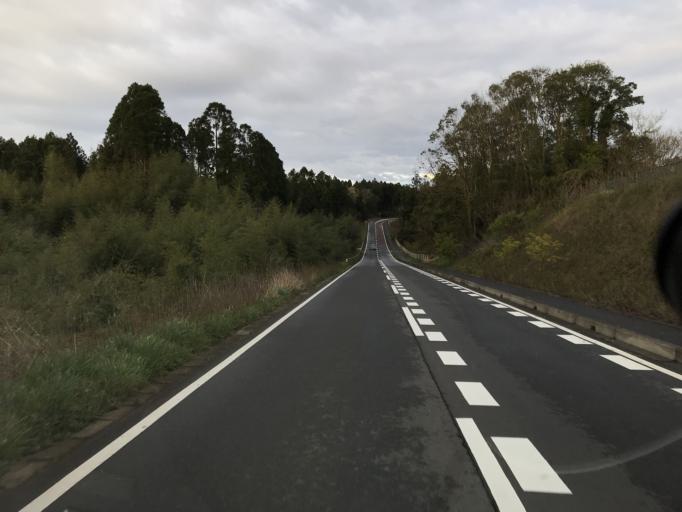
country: JP
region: Chiba
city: Yokaichiba
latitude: 35.7608
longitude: 140.4601
